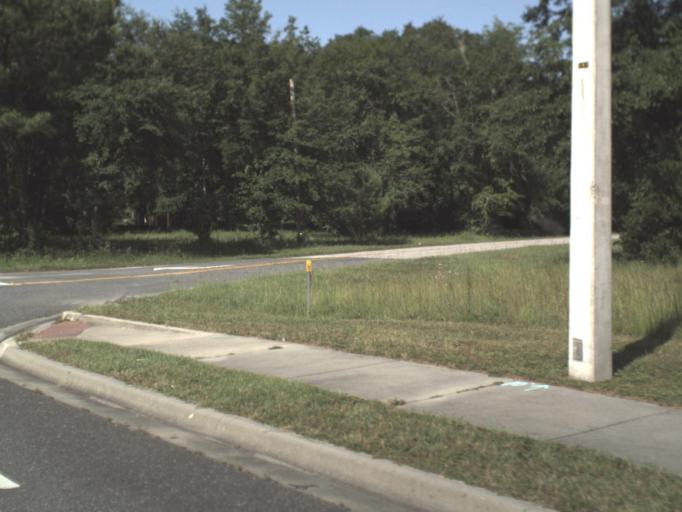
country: US
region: Florida
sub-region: Columbia County
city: Lake City
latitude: 30.1575
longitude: -82.6466
